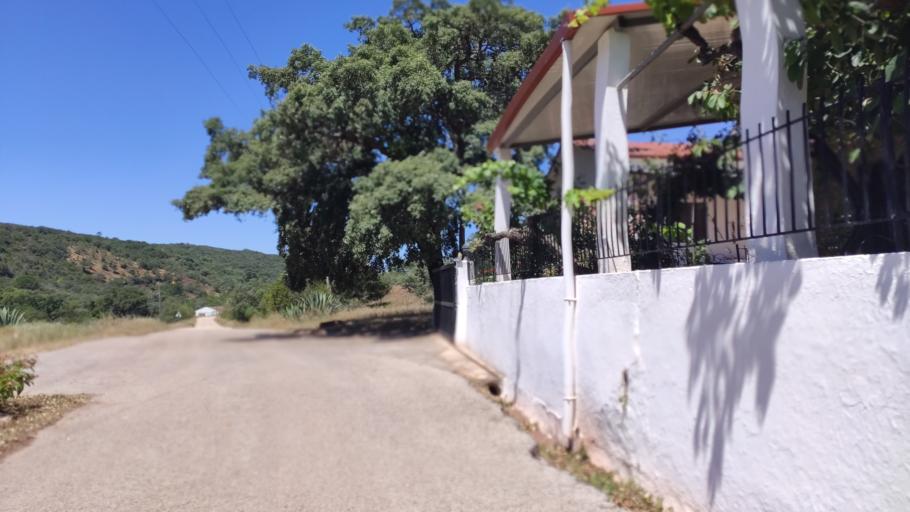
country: PT
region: Faro
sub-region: Sao Bras de Alportel
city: Sao Bras de Alportel
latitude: 37.1740
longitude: -7.9212
